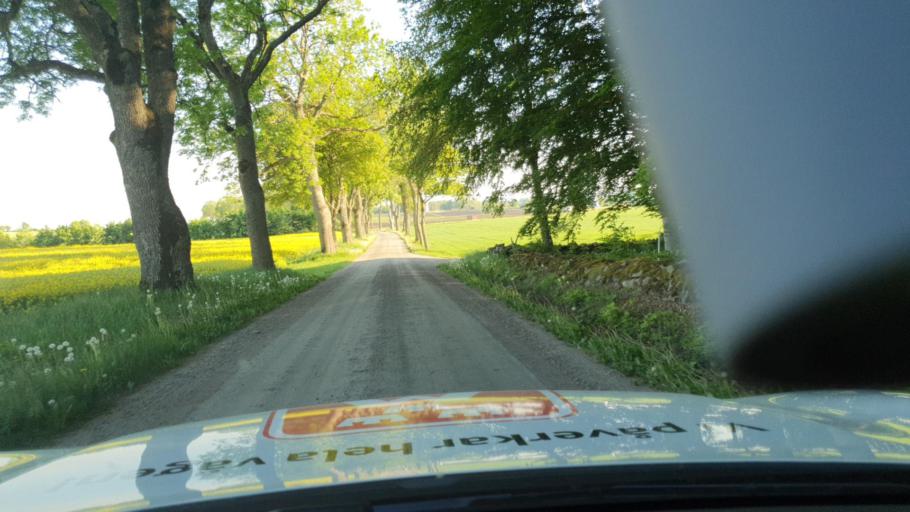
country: SE
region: Vaestra Goetaland
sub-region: Falkopings Kommun
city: Akarp
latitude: 58.1472
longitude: 13.7003
